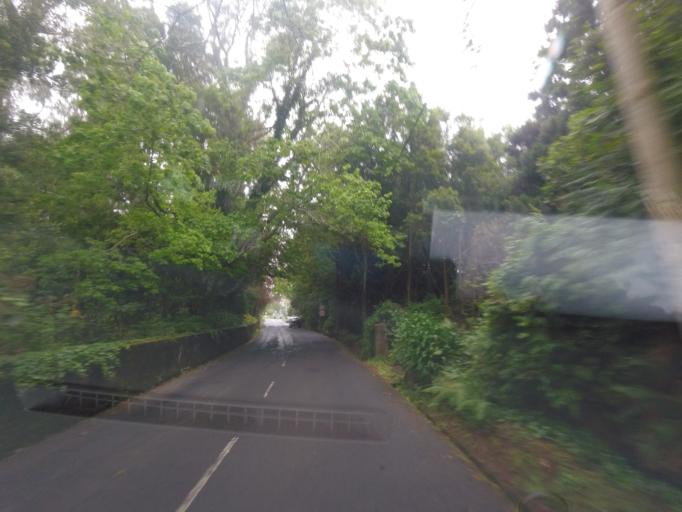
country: PT
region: Madeira
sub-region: Santa Cruz
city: Santa Cruz
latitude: 32.7227
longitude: -16.8158
